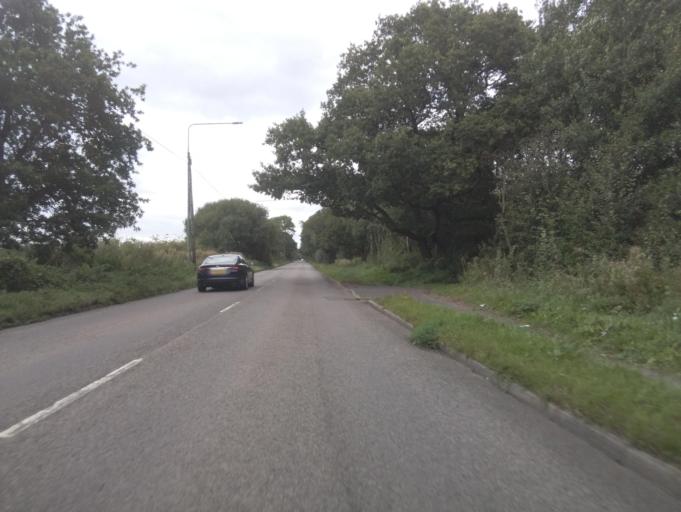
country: GB
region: England
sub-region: Solihull
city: Cheswick Green
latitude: 52.3713
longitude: -1.7850
